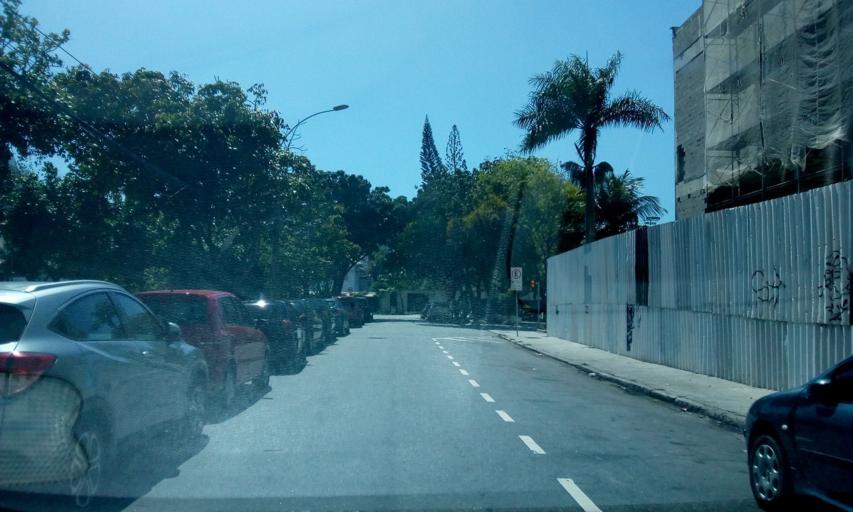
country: BR
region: Rio de Janeiro
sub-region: Rio De Janeiro
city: Rio de Janeiro
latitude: -23.0102
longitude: -43.3219
